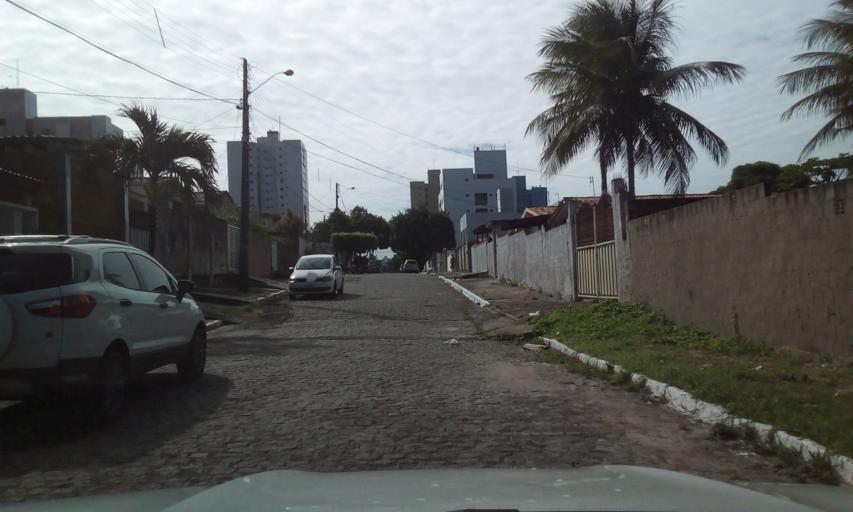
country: BR
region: Paraiba
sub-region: Joao Pessoa
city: Joao Pessoa
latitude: -7.1242
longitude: -34.8504
